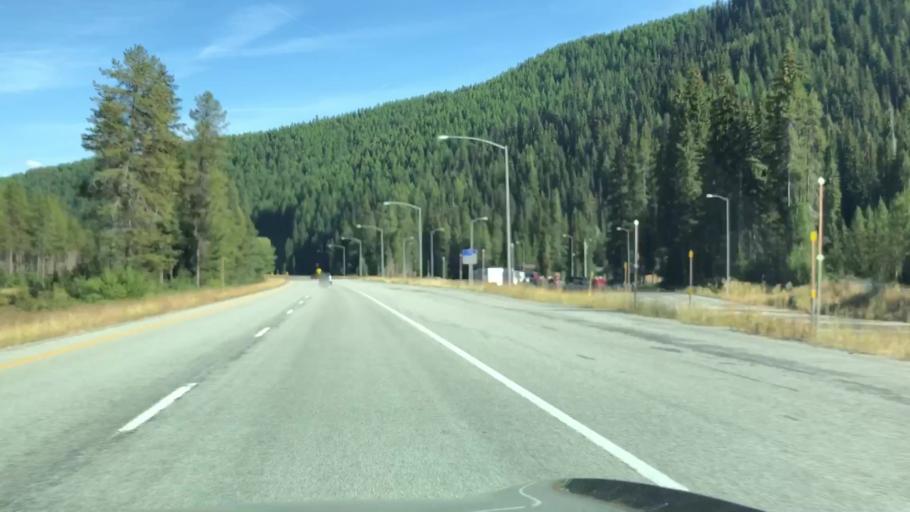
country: US
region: Idaho
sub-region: Shoshone County
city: Wallace
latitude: 47.4208
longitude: -115.6307
